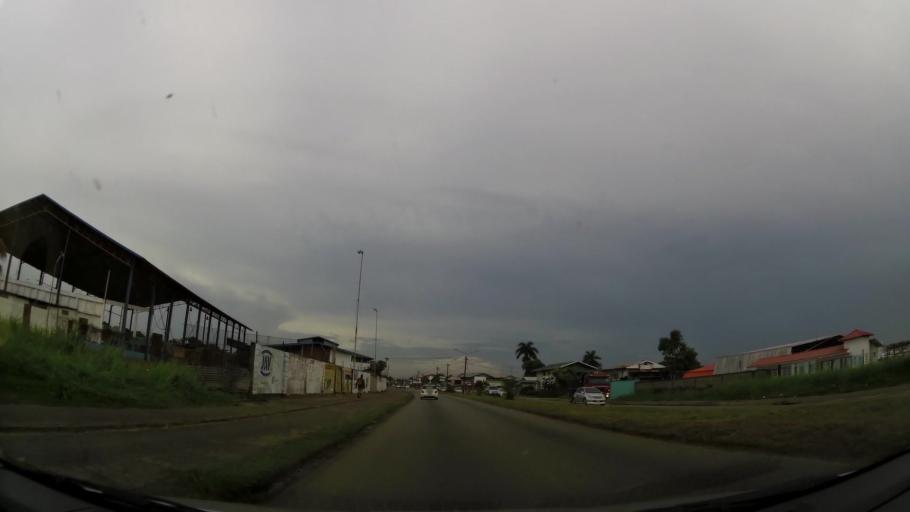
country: SR
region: Paramaribo
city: Paramaribo
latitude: 5.8104
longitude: -55.1870
